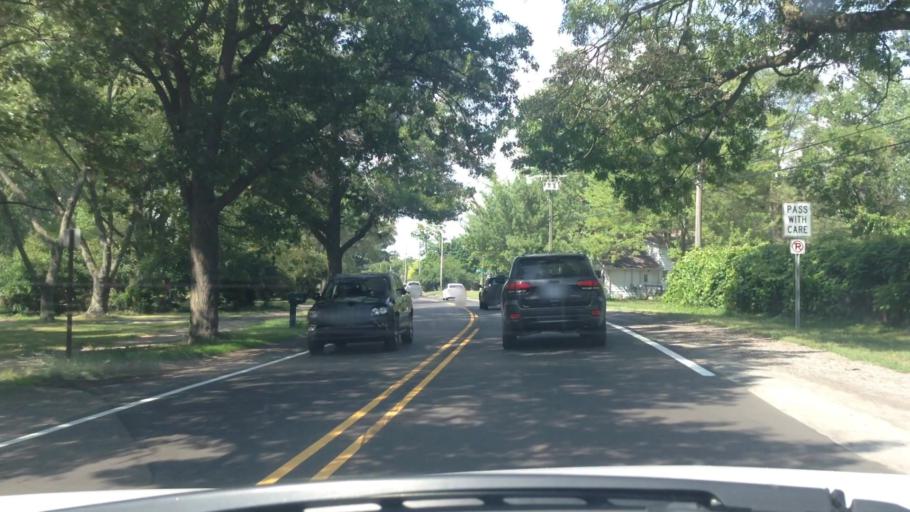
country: US
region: Michigan
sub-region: Oakland County
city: Waterford
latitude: 42.6970
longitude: -83.3714
